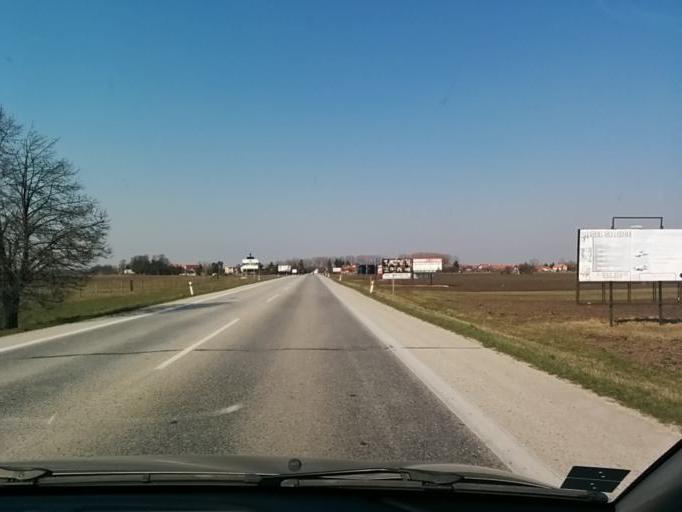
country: SK
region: Trnavsky
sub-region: Okres Galanta
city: Galanta
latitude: 48.2118
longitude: 17.7297
